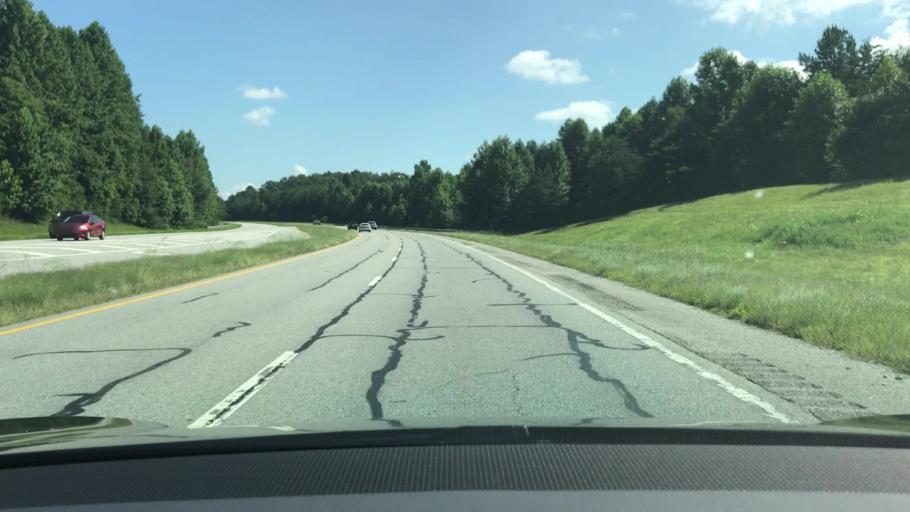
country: US
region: Georgia
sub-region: Habersham County
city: Clarkesville
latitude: 34.6598
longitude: -83.4351
